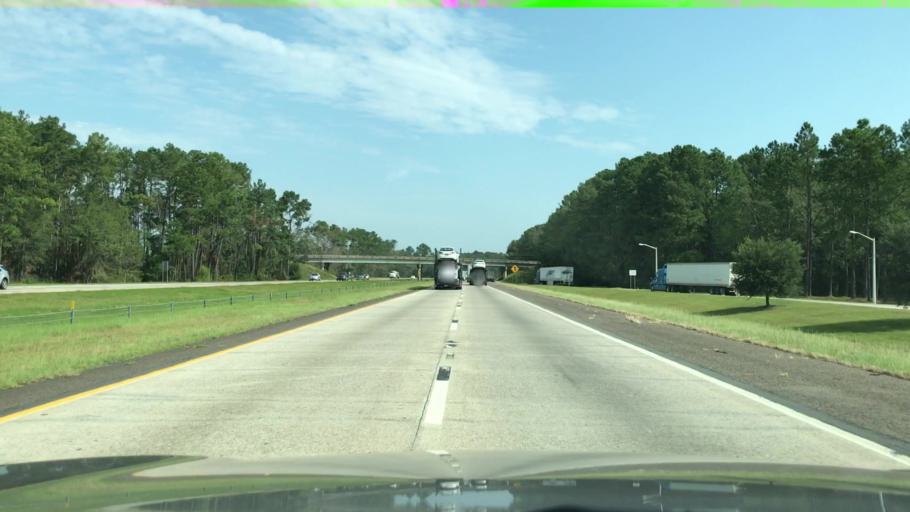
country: US
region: South Carolina
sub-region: Hampton County
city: Yemassee
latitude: 32.8029
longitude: -80.7706
